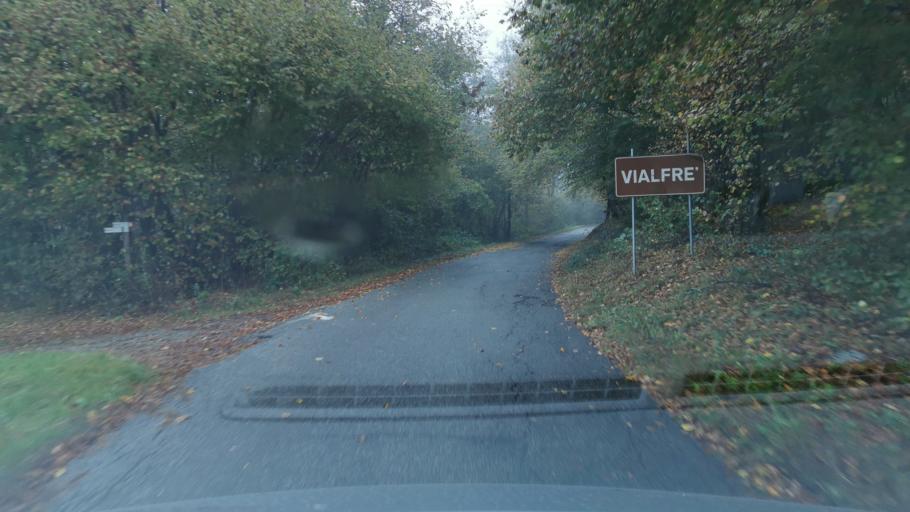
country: IT
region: Piedmont
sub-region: Provincia di Torino
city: Vialfre
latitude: 45.3723
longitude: 7.8089
